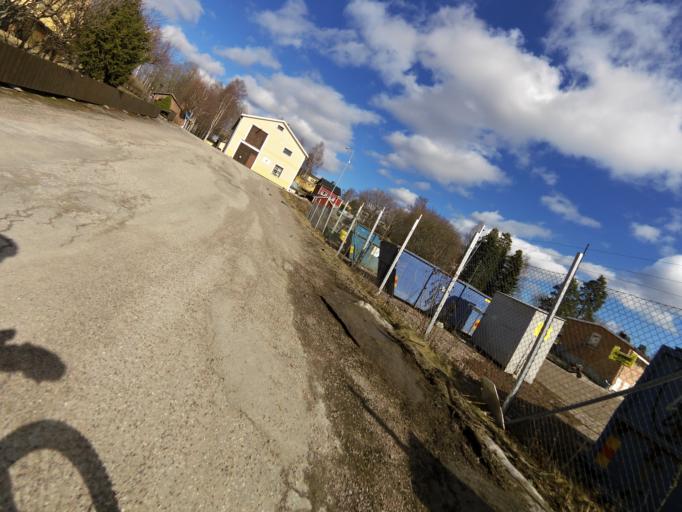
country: SE
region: Gaevleborg
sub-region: Hofors Kommun
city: Hofors
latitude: 60.5398
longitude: 16.2870
